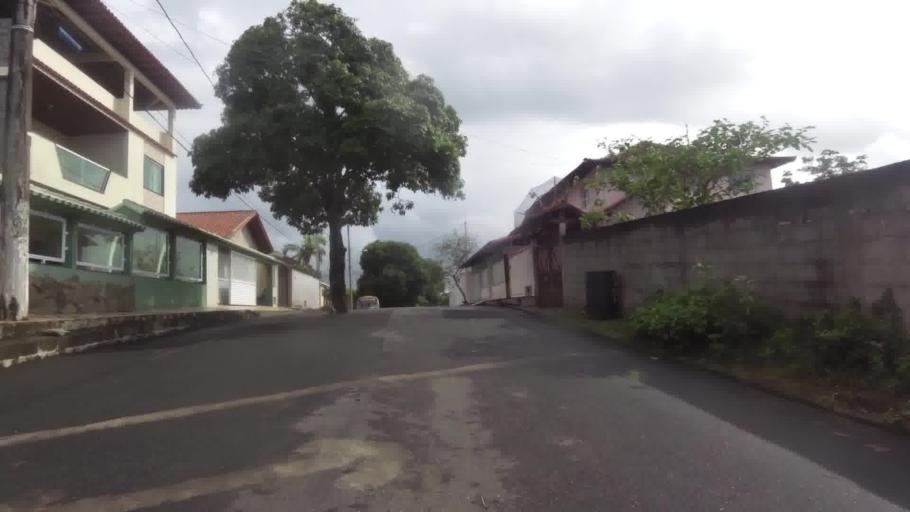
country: BR
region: Espirito Santo
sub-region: Piuma
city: Piuma
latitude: -20.8318
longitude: -40.7043
